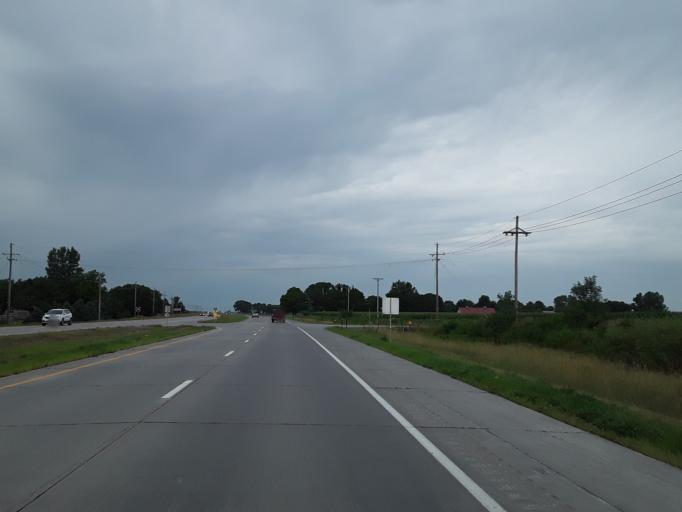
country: US
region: Nebraska
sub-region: Washington County
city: Blair
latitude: 41.4645
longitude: -96.1398
